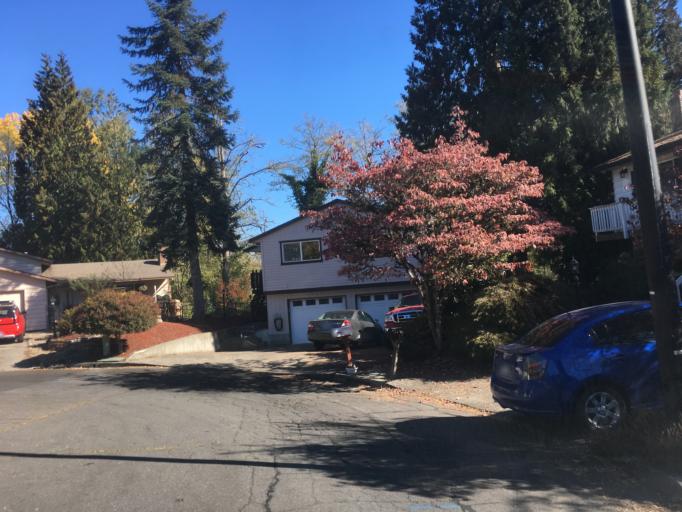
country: US
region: Oregon
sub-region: Multnomah County
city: Gresham
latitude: 45.4819
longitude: -122.4199
